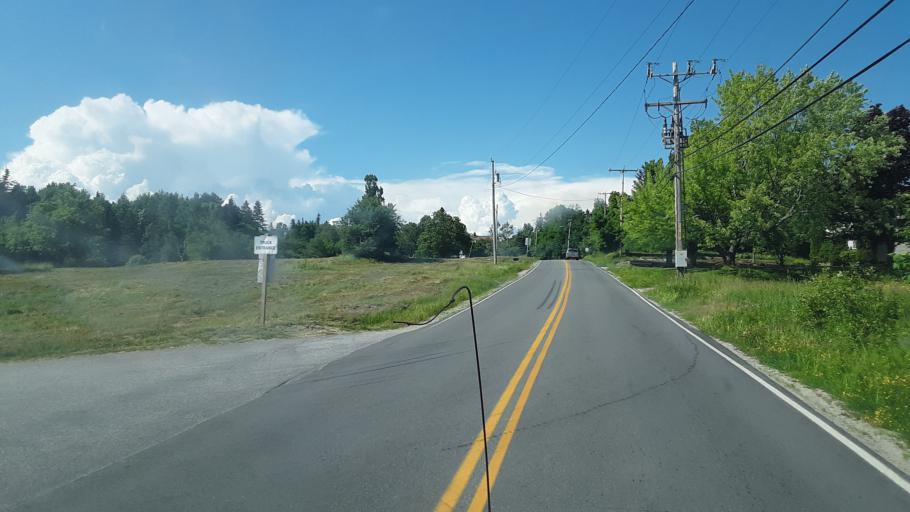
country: US
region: Maine
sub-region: Washington County
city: Cherryfield
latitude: 44.6102
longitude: -67.9249
